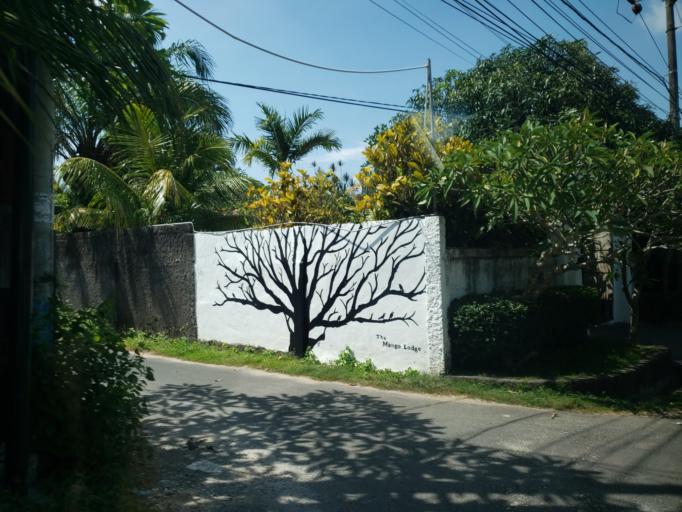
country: ID
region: Bali
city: Kangin
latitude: -8.8226
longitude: 115.1525
